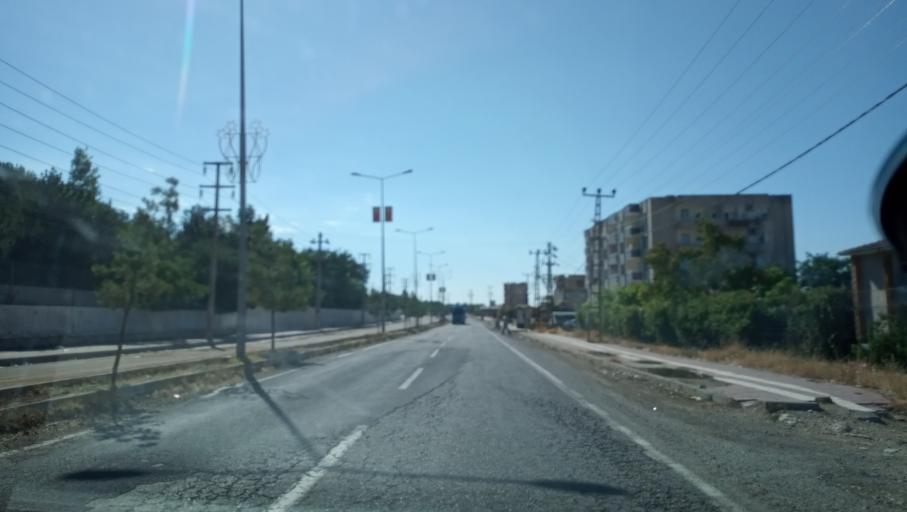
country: TR
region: Diyarbakir
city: Silvan
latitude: 38.1370
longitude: 41.0228
